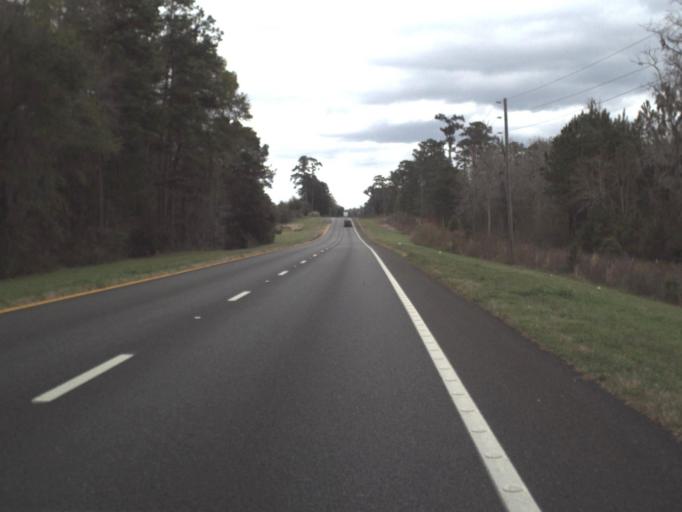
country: US
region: Florida
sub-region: Leon County
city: Tallahassee
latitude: 30.6018
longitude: -84.1824
